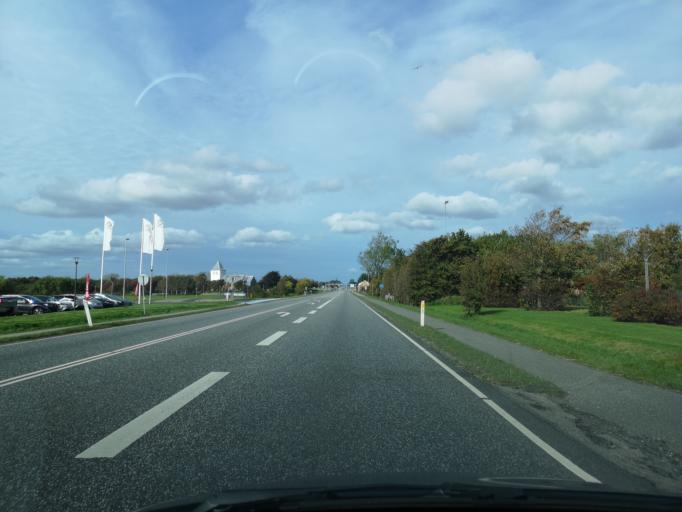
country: DK
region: Central Jutland
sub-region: Holstebro Kommune
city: Holstebro
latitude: 56.3827
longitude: 8.6131
